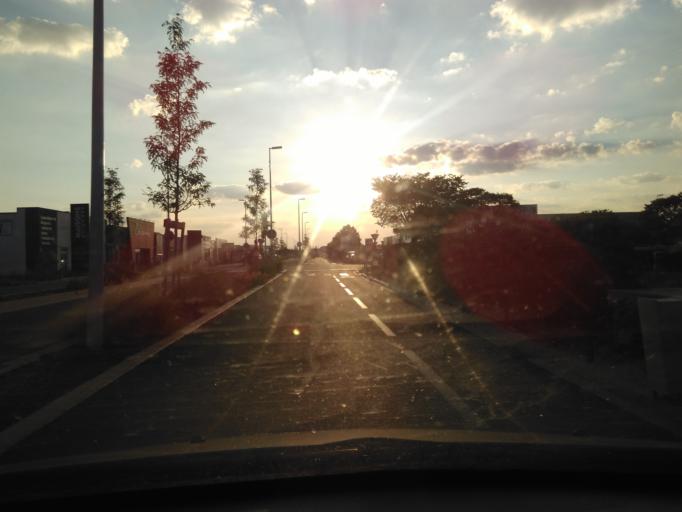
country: FR
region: Poitou-Charentes
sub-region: Departement de la Charente-Maritime
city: Puilboreau
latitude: 46.1767
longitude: -1.1089
